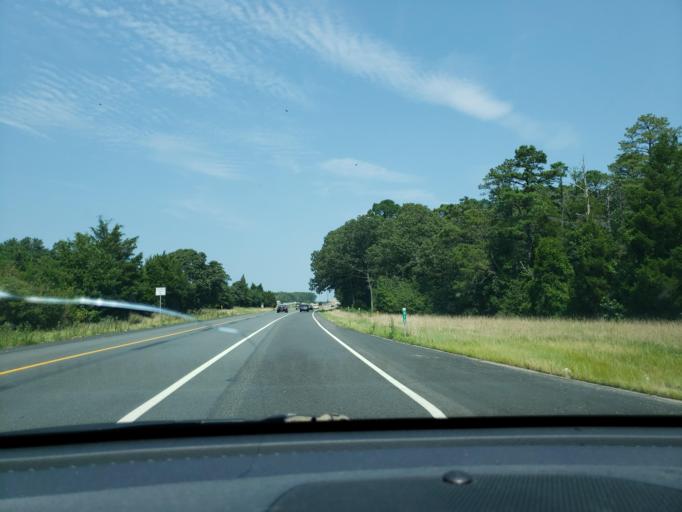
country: US
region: New Jersey
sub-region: Atlantic County
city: Somers Point
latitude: 39.3380
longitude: -74.6059
